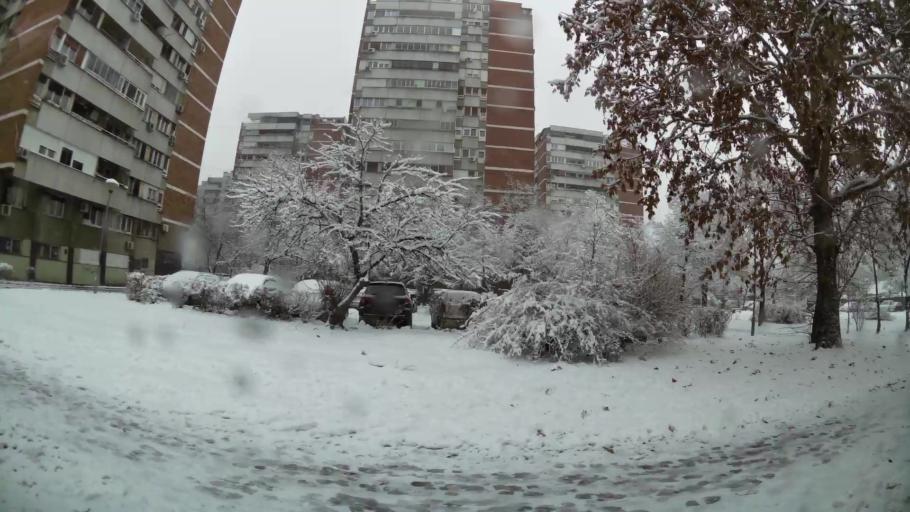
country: RS
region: Central Serbia
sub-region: Belgrade
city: Cukarica
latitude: 44.7993
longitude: 20.3772
